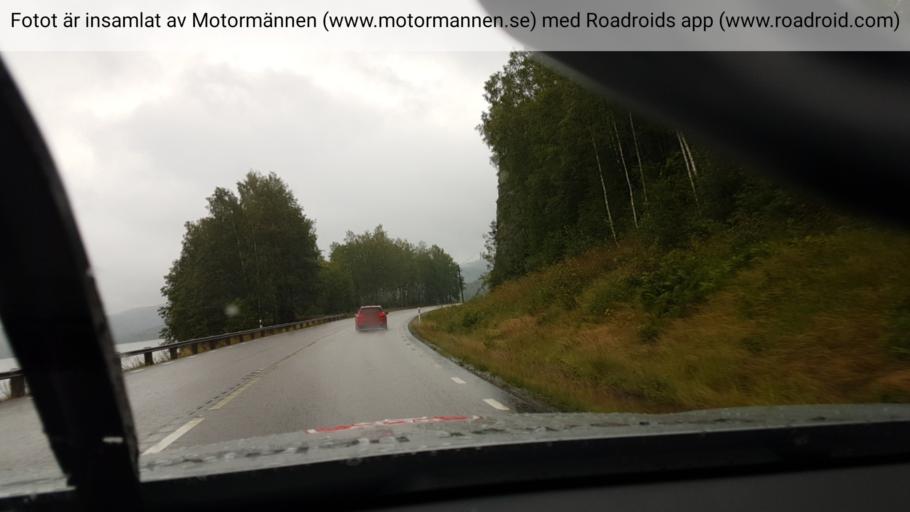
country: SE
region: Vaestra Goetaland
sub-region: Bengtsfors Kommun
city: Dals Langed
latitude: 59.0552
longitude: 12.4407
